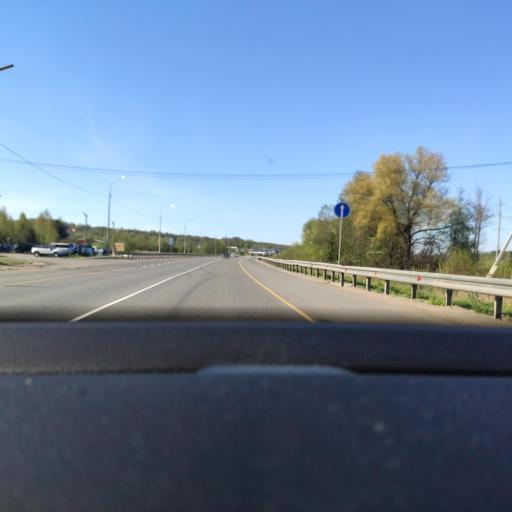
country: RU
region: Moskovskaya
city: Yakhroma
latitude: 56.3042
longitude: 37.4801
